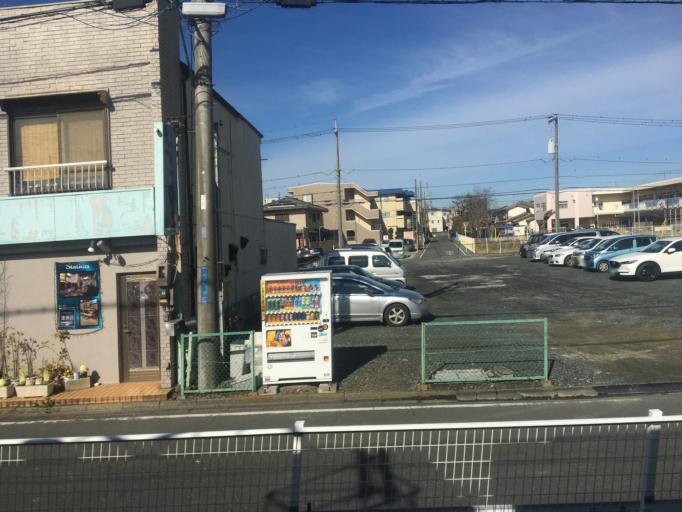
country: JP
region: Saitama
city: Sakado
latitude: 35.9736
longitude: 139.3977
